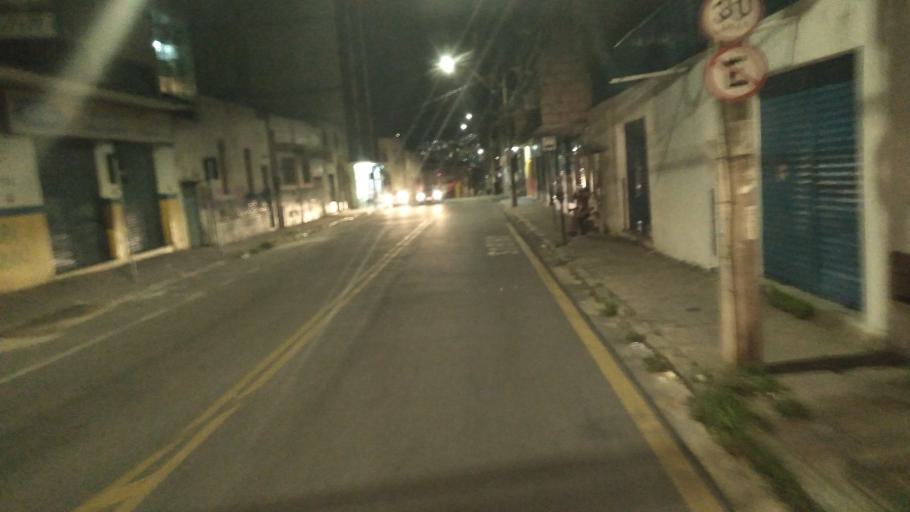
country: BR
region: Minas Gerais
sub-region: Belo Horizonte
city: Belo Horizonte
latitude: -19.9071
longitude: -43.9459
